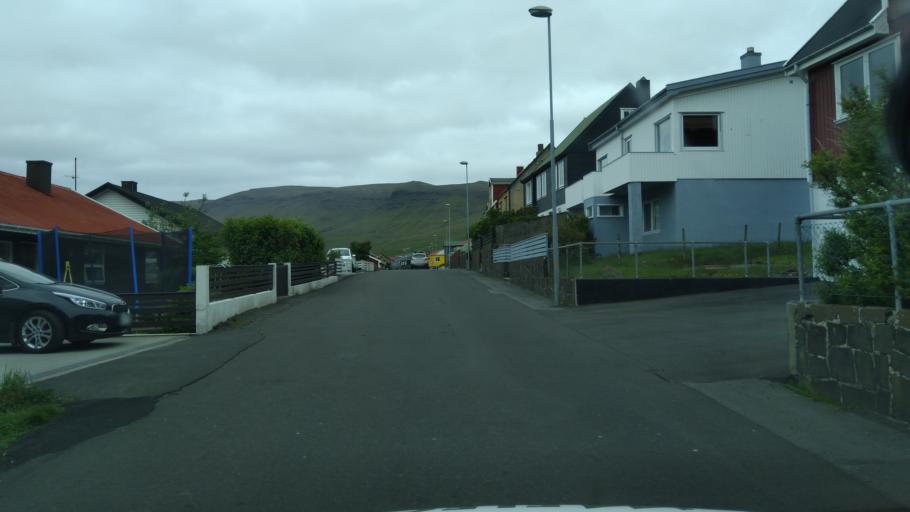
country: FO
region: Suduroy
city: Tvoroyri
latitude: 61.5626
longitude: -6.8338
